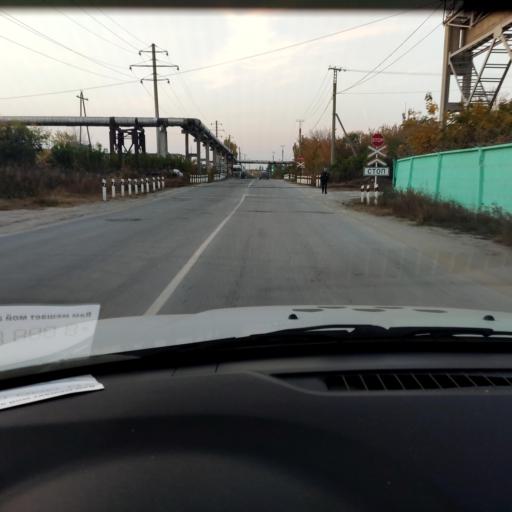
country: RU
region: Samara
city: Tol'yatti
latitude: 53.5331
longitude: 49.4634
